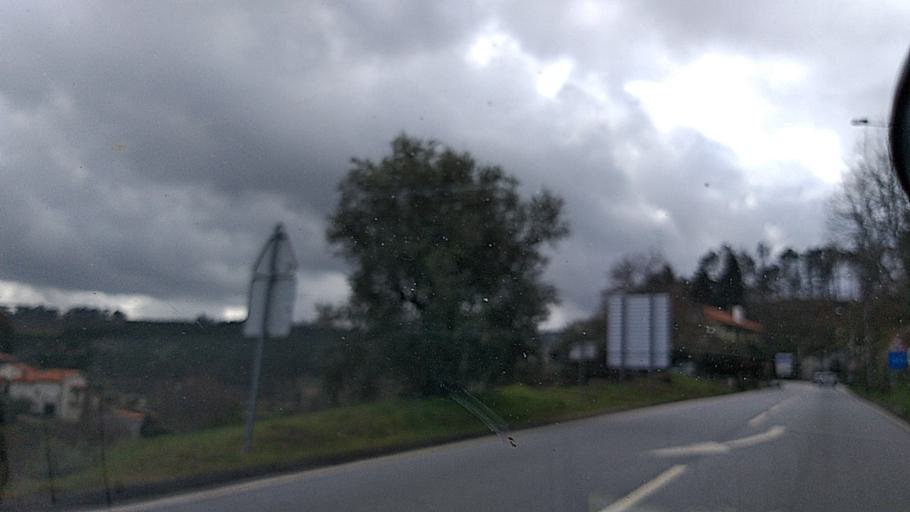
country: PT
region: Viseu
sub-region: Mangualde
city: Mangualde
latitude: 40.6375
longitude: -7.7400
